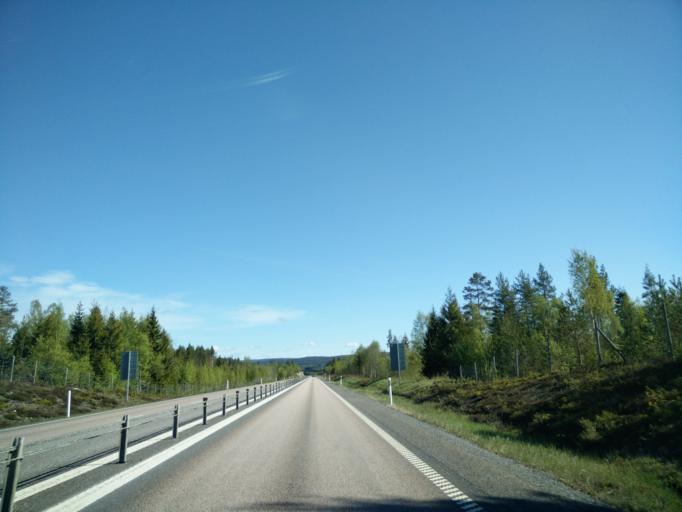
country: SE
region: Vaesternorrland
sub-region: Kramfors Kommun
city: Nordingra
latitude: 62.8856
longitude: 18.0864
